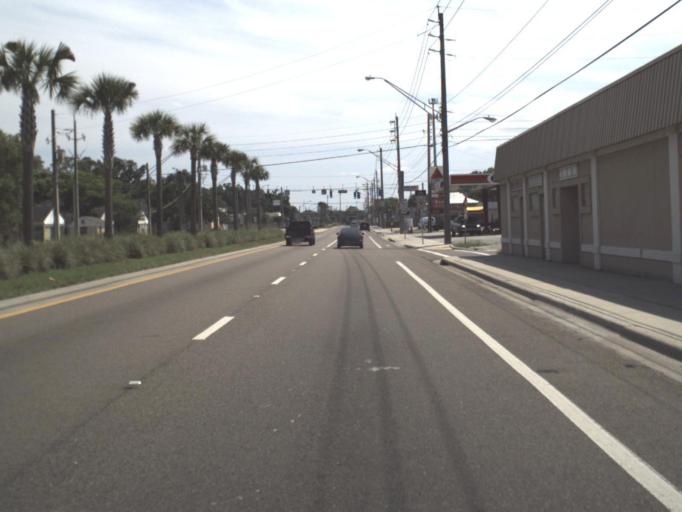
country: US
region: Florida
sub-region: Duval County
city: Jacksonville
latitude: 30.3820
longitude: -81.6499
